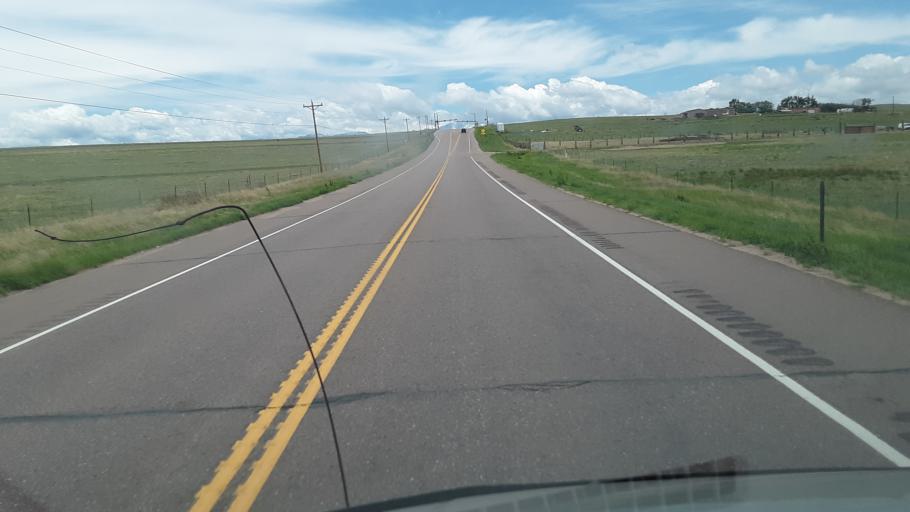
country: US
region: Colorado
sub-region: El Paso County
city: Cimarron Hills
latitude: 38.8386
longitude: -104.5472
